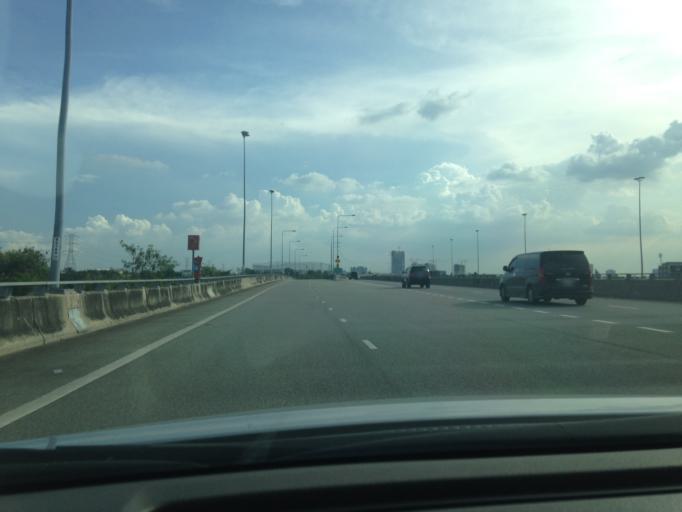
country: TH
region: Bangkok
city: Don Mueang
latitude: 13.9437
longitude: 100.5621
